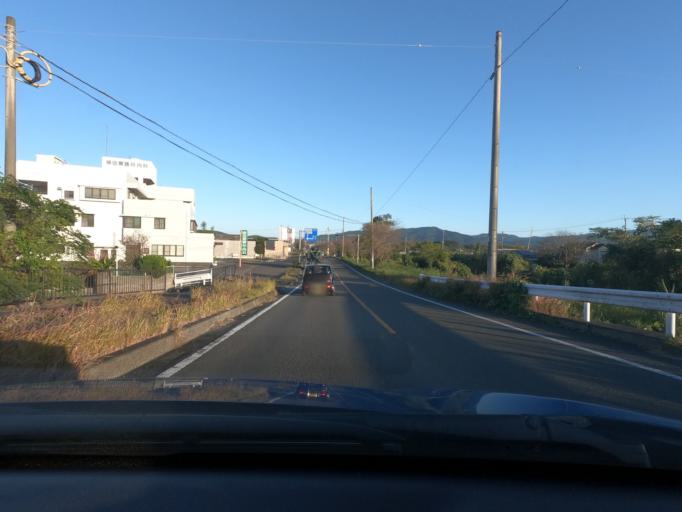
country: JP
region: Kagoshima
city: Satsumasendai
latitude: 31.8103
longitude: 130.3148
